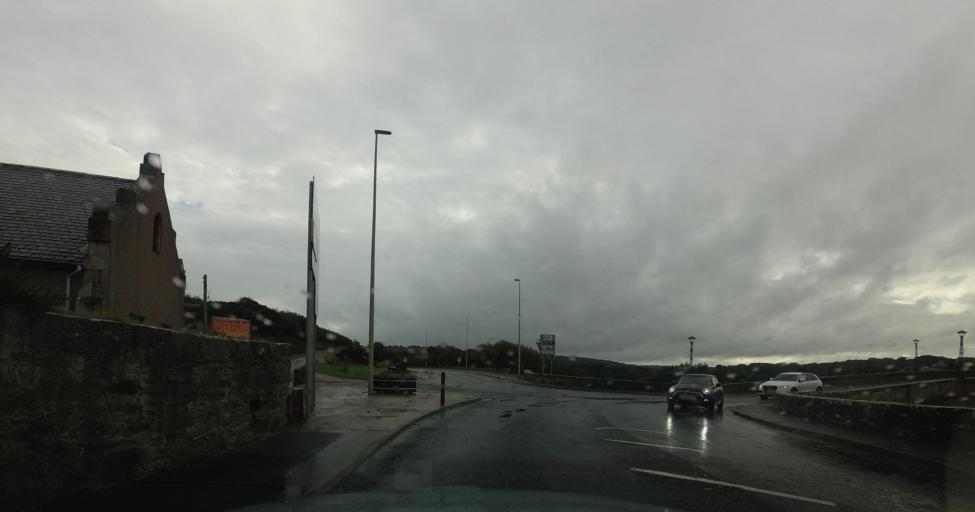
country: GB
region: Scotland
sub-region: Aberdeenshire
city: Macduff
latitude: 57.6630
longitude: -2.5118
